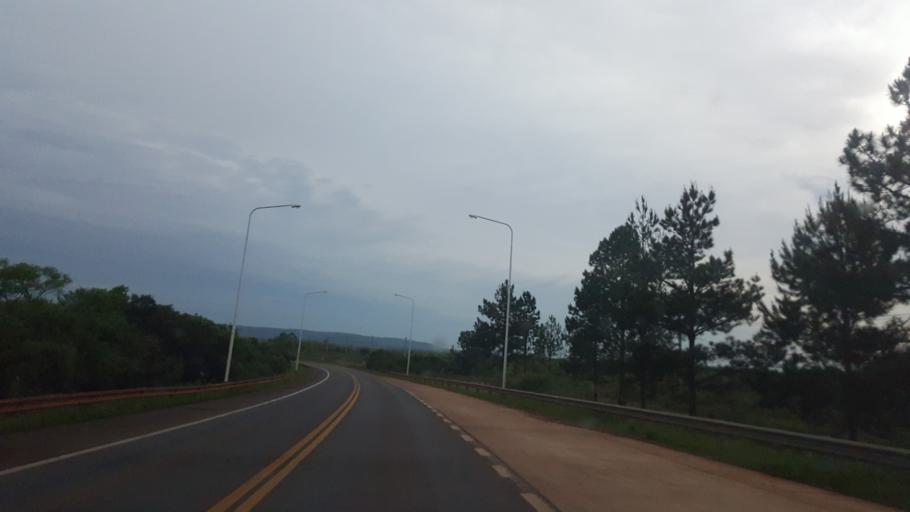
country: AR
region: Misiones
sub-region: Departamento de Apostoles
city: San Jose
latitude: -27.7799
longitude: -55.8129
